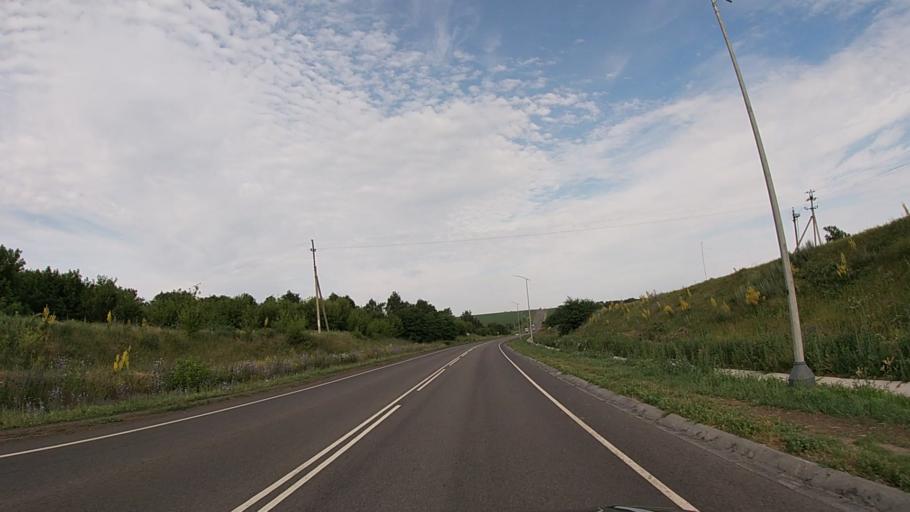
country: RU
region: Belgorod
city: Severnyy
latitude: 50.6644
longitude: 36.5266
